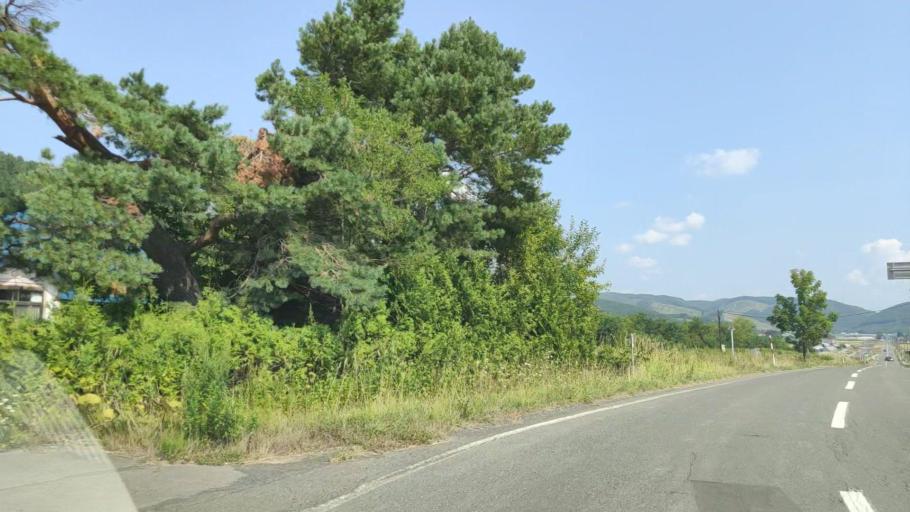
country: JP
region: Hokkaido
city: Shimo-furano
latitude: 43.3945
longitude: 142.3910
